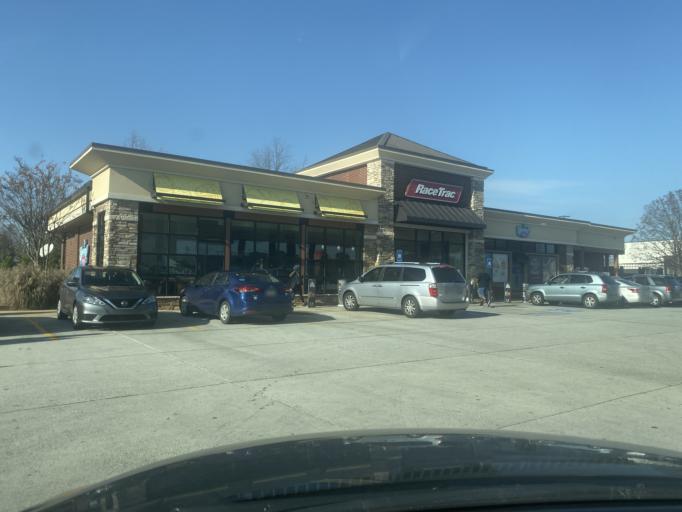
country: US
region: Georgia
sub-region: Henry County
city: McDonough
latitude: 33.4251
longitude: -84.1844
